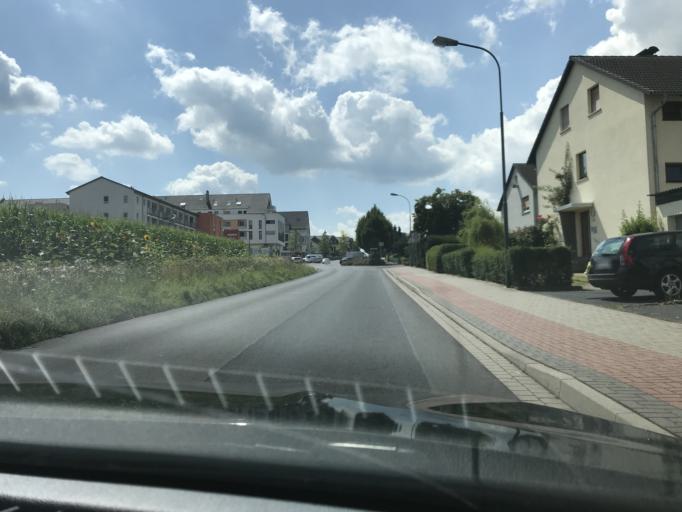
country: DE
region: Hesse
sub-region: Regierungsbezirk Kassel
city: Kunzell
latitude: 50.5417
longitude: 9.7143
